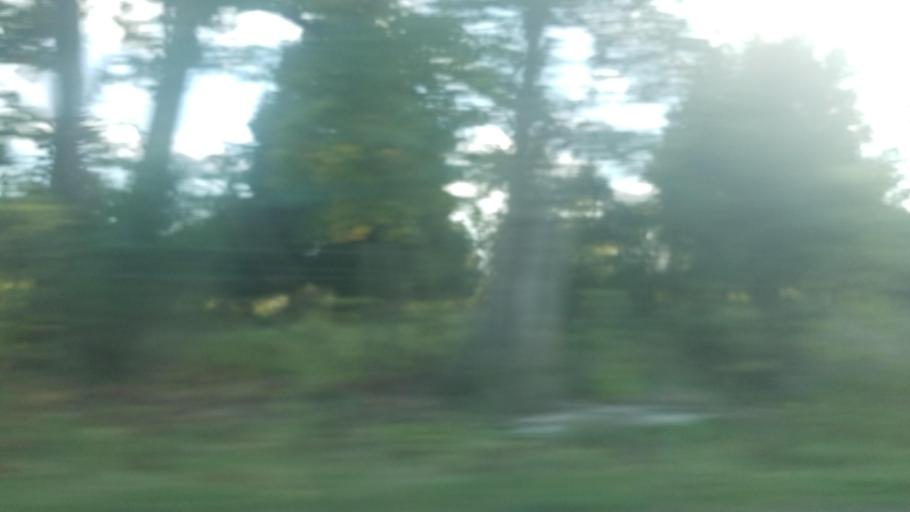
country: US
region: Illinois
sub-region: Saline County
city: Carrier Mills
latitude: 37.7716
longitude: -88.7513
